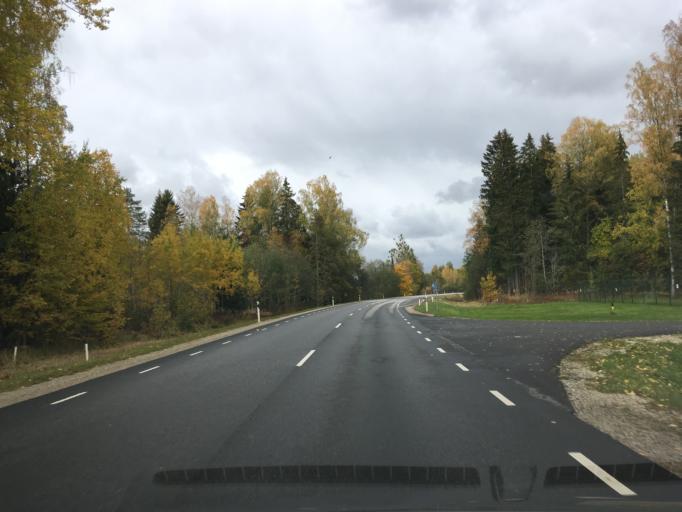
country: EE
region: Harju
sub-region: Anija vald
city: Kehra
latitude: 59.2988
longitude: 25.3636
